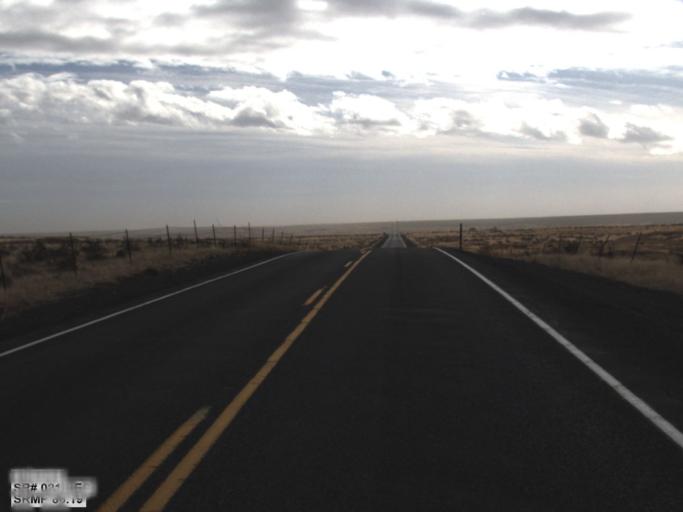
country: US
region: Washington
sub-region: Okanogan County
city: Coulee Dam
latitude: 47.6864
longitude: -118.7219
